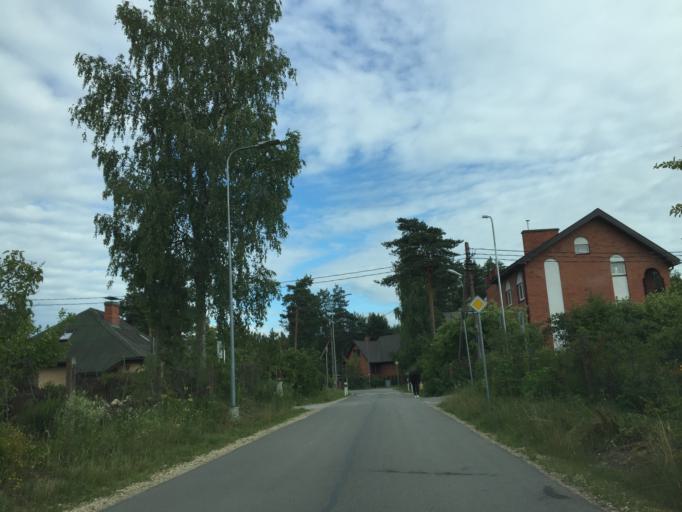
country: LV
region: Carnikava
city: Carnikava
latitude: 57.1329
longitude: 24.2520
